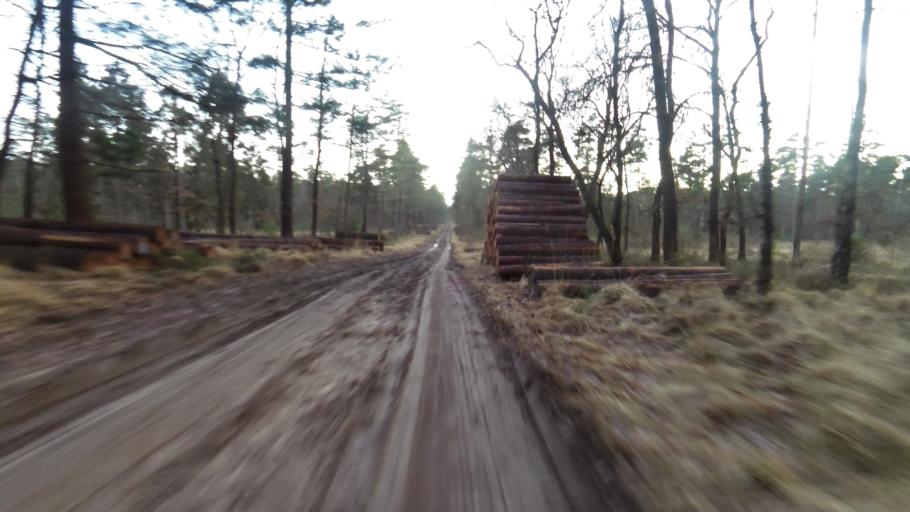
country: NL
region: Gelderland
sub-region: Gemeente Apeldoorn
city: Uddel
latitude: 52.2716
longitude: 5.8462
